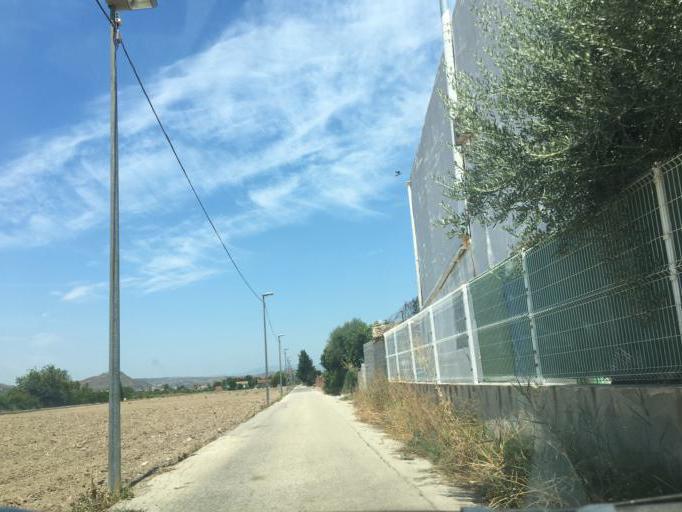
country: ES
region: Murcia
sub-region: Murcia
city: Santomera
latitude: 38.0159
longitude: -1.0543
